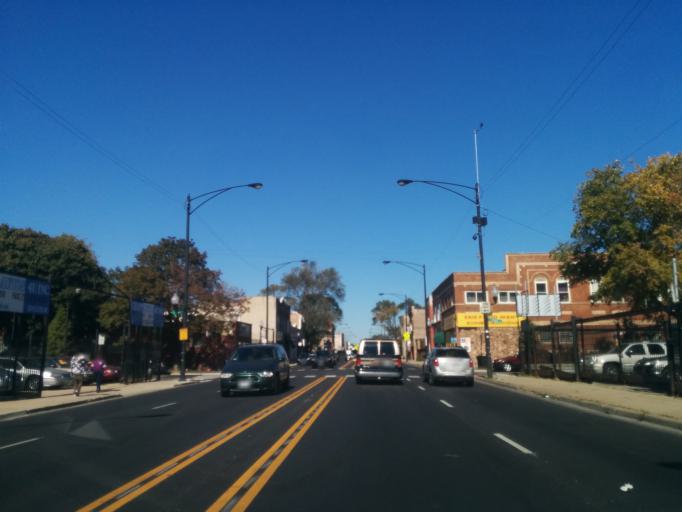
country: US
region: Illinois
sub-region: Cook County
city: Oak Park
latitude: 41.8916
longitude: -87.7457
